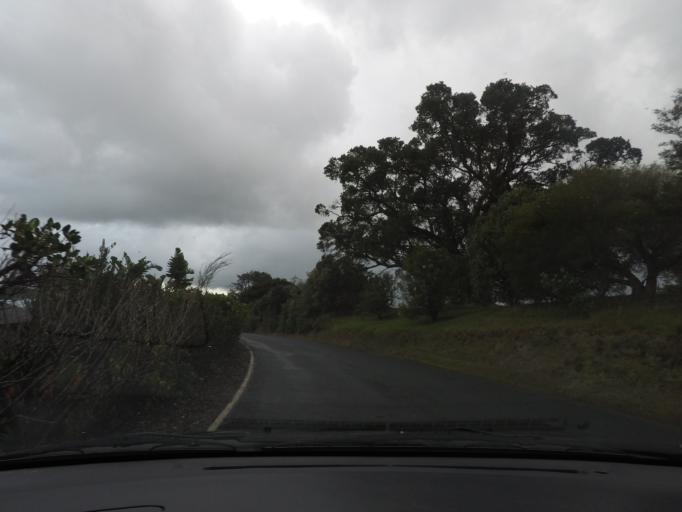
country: NZ
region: Auckland
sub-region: Auckland
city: Warkworth
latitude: -36.4747
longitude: 174.7340
